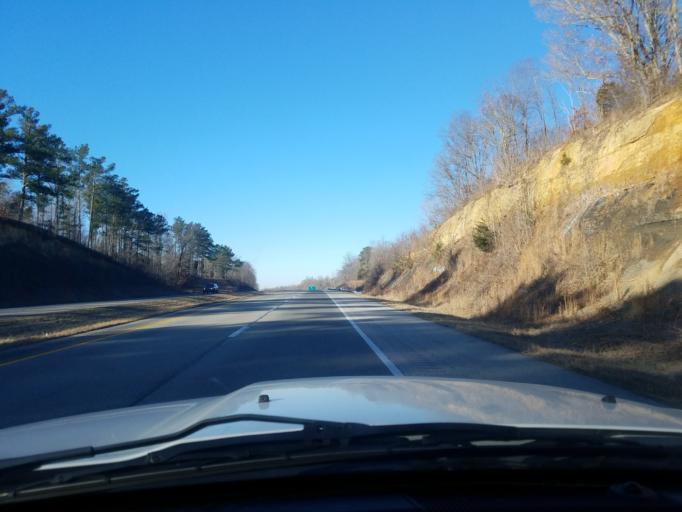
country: US
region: Kentucky
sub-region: Ohio County
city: Oak Grove
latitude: 37.3933
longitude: -86.7805
